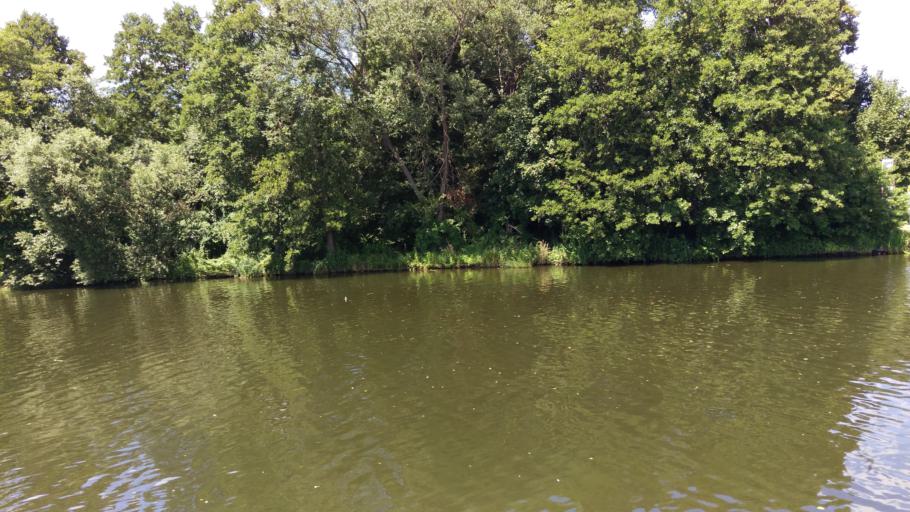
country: DE
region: Brandenburg
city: Brandenburg an der Havel
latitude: 52.4201
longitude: 12.5918
